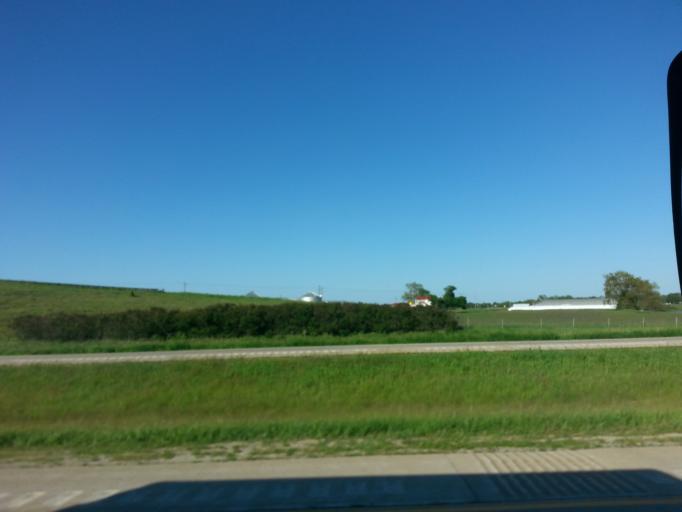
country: US
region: Illinois
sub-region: Woodford County
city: El Paso
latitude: 40.6781
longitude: -89.0275
